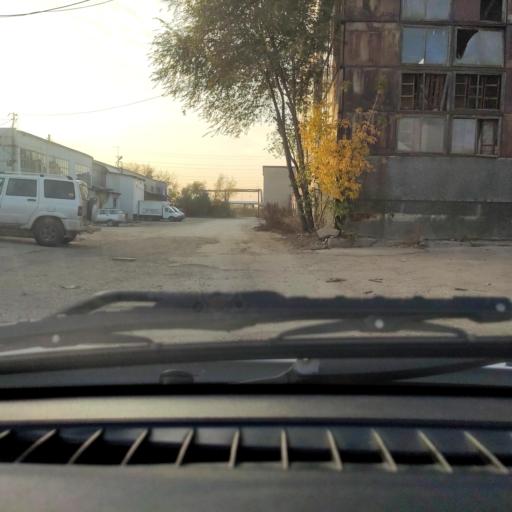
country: RU
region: Samara
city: Tol'yatti
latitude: 53.5286
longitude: 49.4635
